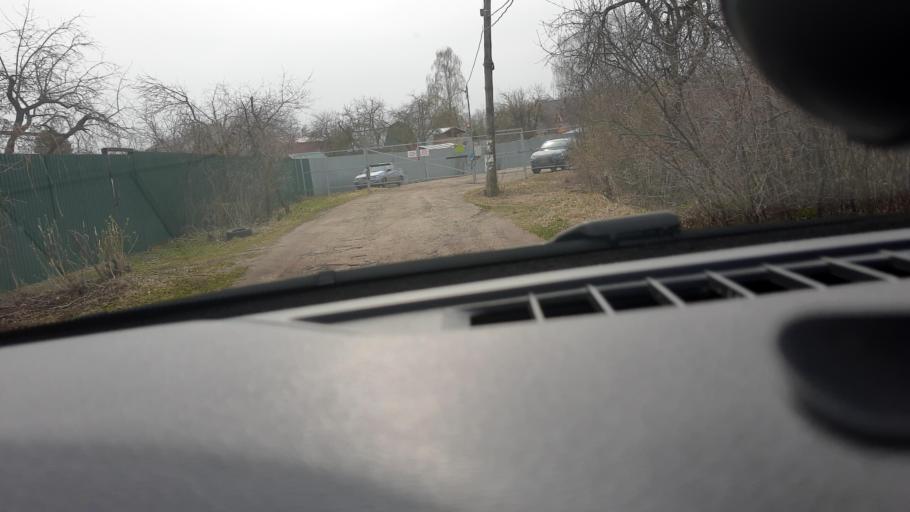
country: RU
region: Nizjnij Novgorod
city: Gorbatovka
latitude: 56.3842
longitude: 43.8207
